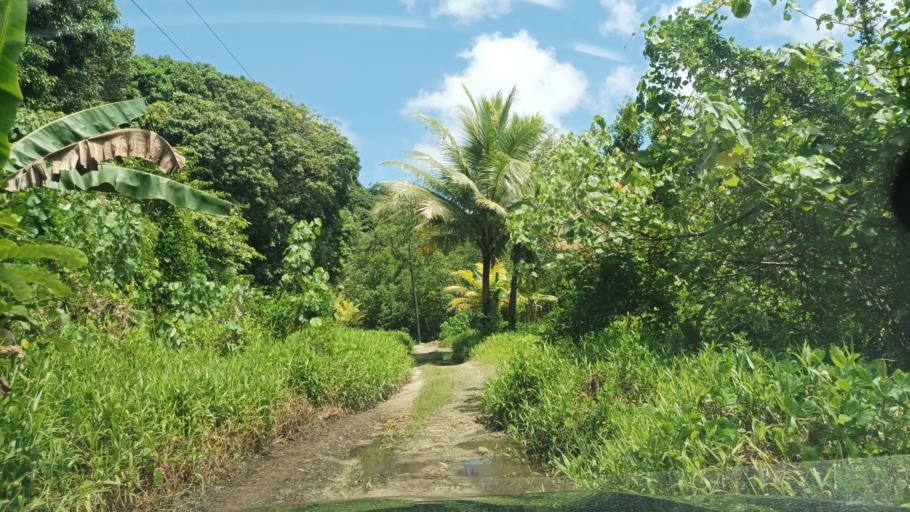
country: FM
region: Pohnpei
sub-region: Sokehs Municipality
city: Palikir - National Government Center
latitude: 6.9473
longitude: 158.1595
